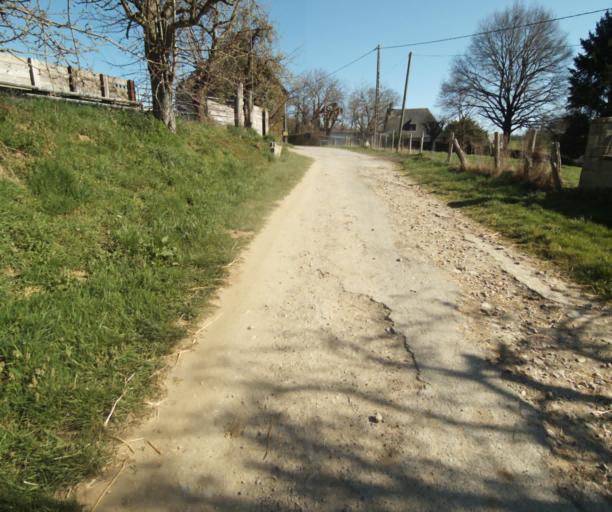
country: FR
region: Limousin
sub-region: Departement de la Correze
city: Chamboulive
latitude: 45.4821
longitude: 1.7359
